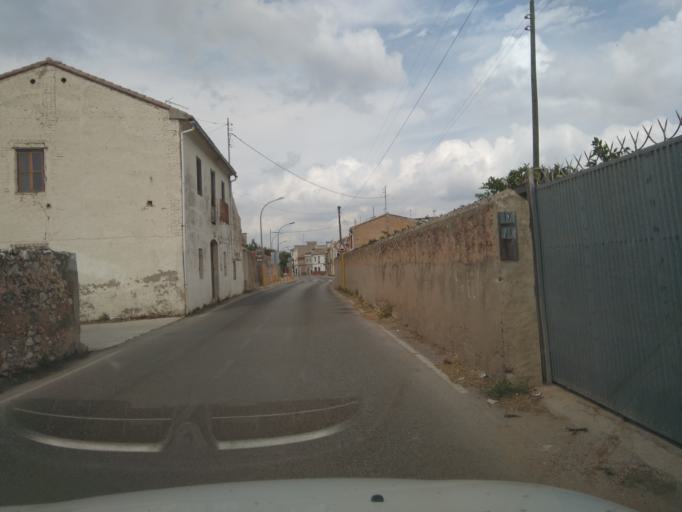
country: ES
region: Valencia
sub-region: Provincia de Valencia
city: Carcaixent
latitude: 39.1146
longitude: -0.4387
